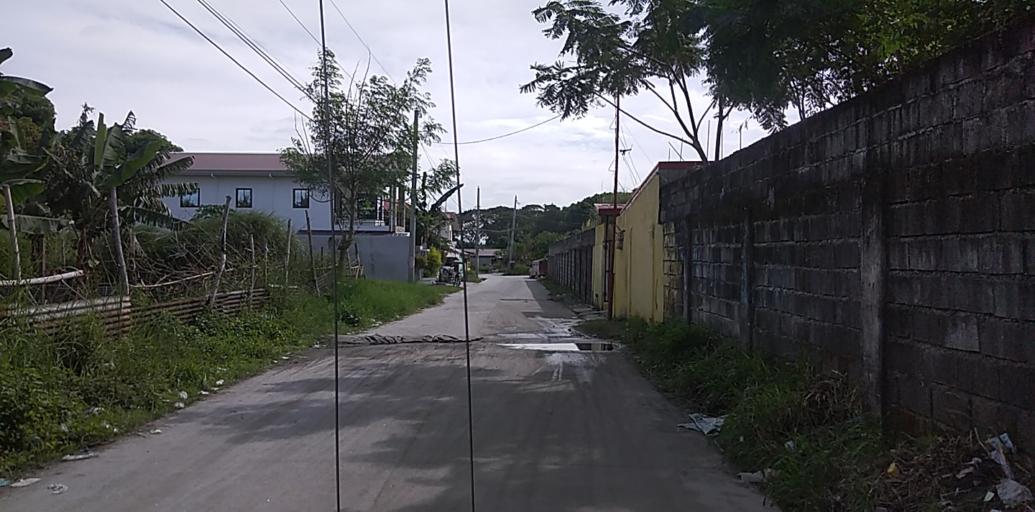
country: PH
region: Central Luzon
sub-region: Province of Pampanga
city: Angeles City
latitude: 15.1299
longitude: 120.5585
